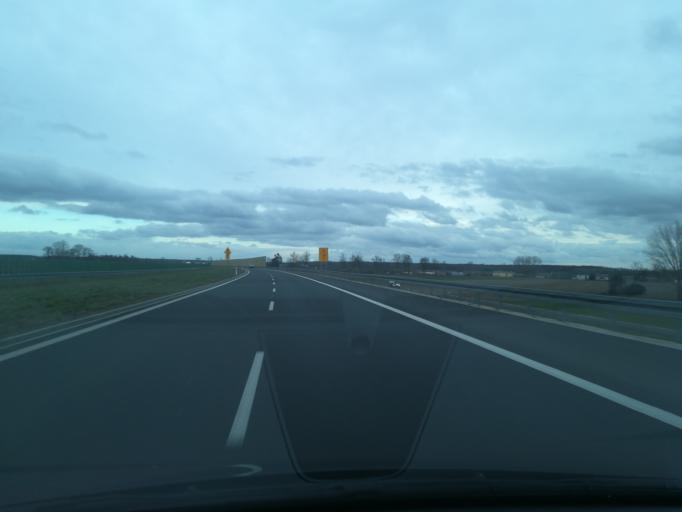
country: PL
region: Lodz Voivodeship
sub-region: Powiat kutnowski
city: Lanieta
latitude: 52.3871
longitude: 19.2949
